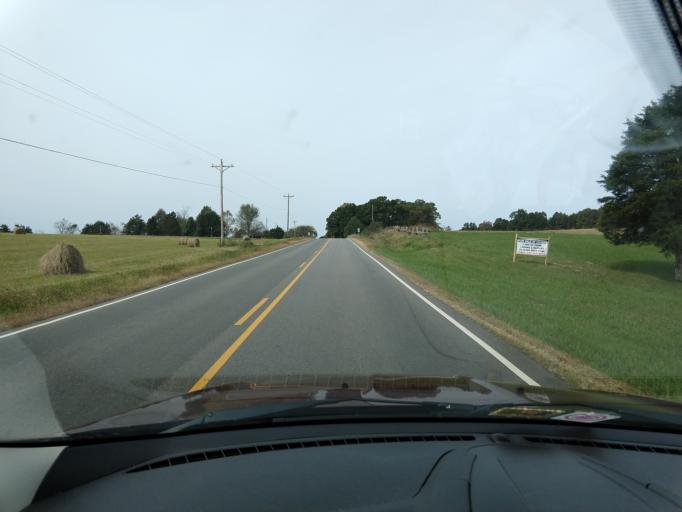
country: US
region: Virginia
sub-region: Franklin County
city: Union Hall
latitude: 36.9655
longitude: -79.5849
